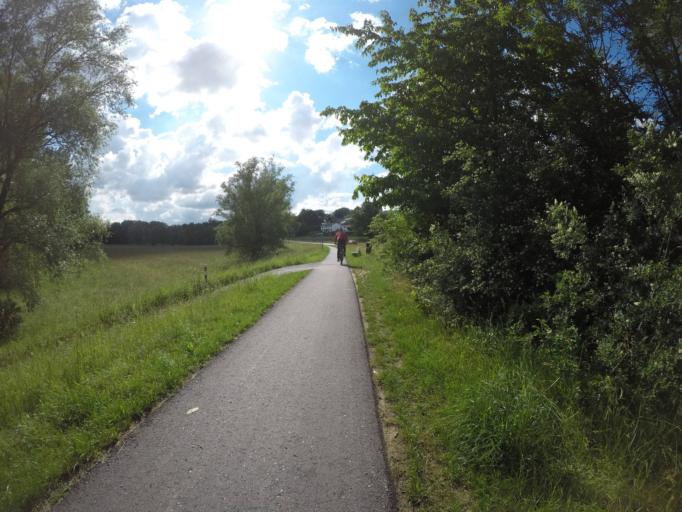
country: DE
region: Bavaria
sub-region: Lower Bavaria
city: Marklkofen
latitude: 48.5722
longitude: 12.5824
